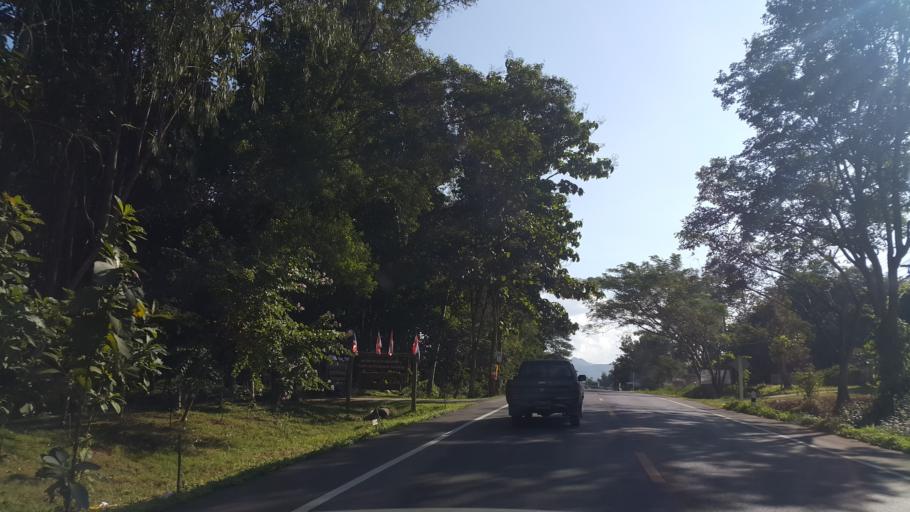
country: TH
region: Lamphun
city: Mae Tha
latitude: 18.5026
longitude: 99.2002
